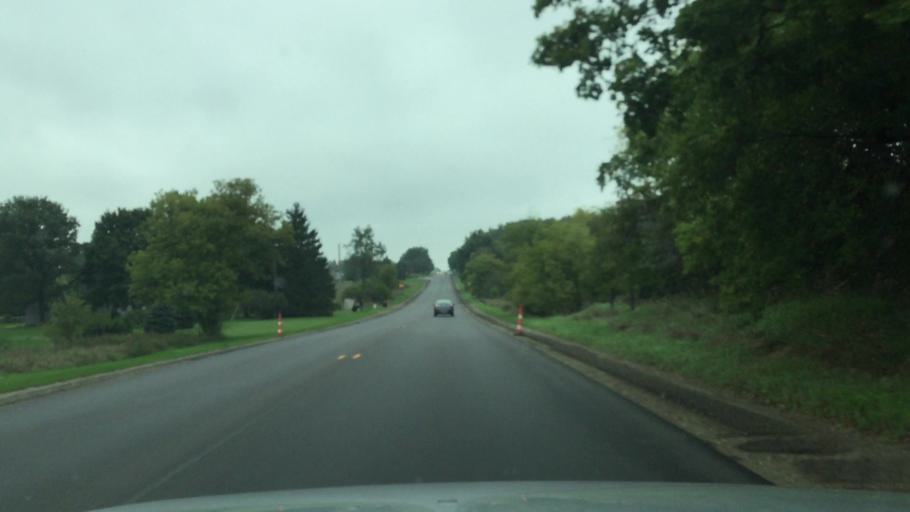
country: US
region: Michigan
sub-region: Shiawassee County
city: Perry
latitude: 42.8527
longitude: -84.2205
